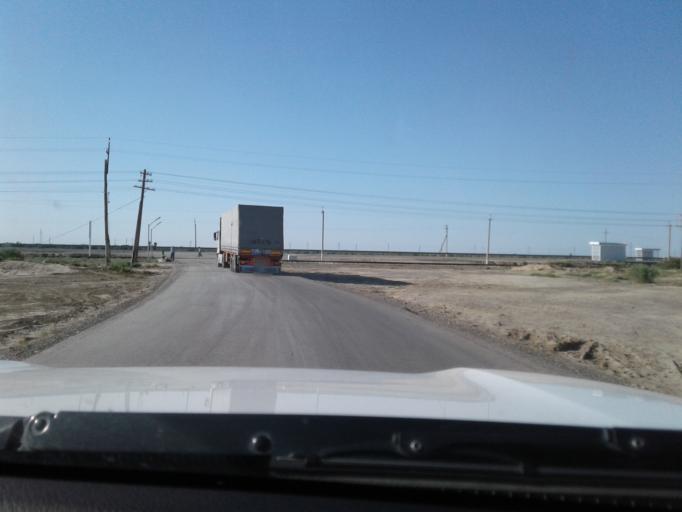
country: IR
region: Razavi Khorasan
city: Kalat-e Naderi
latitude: 37.2021
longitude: 60.0425
